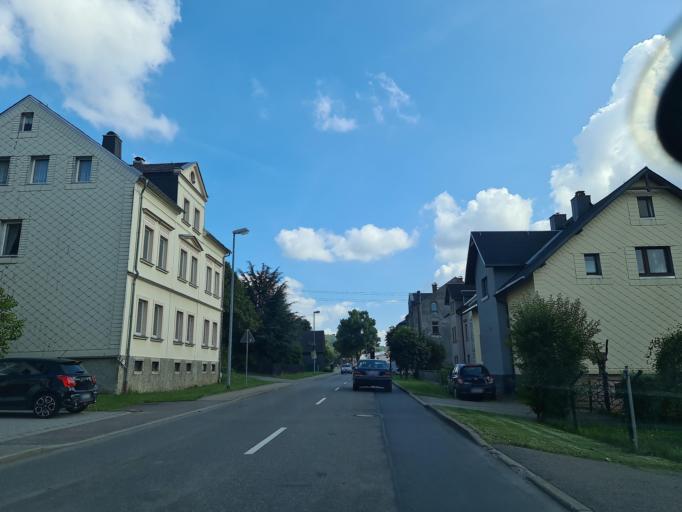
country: DE
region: Saxony
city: Olbernhau
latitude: 50.6488
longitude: 13.3797
